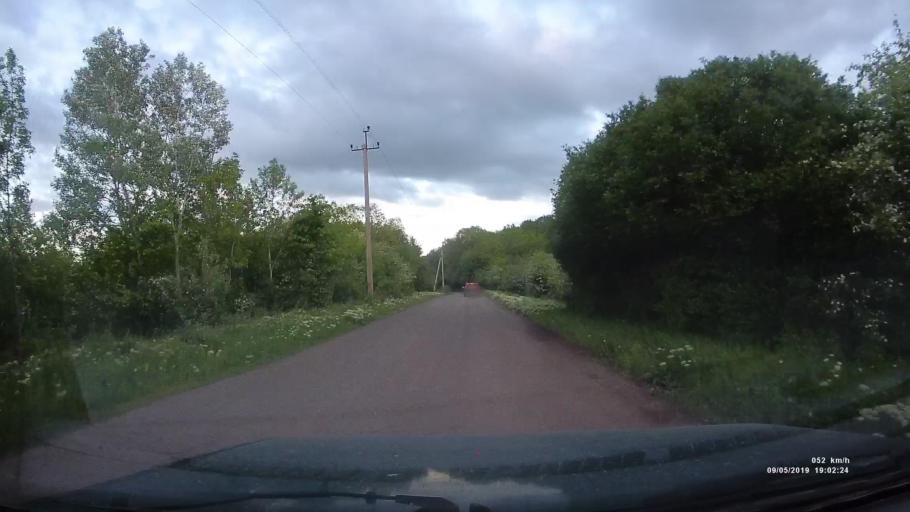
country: RU
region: Krasnodarskiy
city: Kanelovskaya
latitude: 46.7451
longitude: 39.1527
